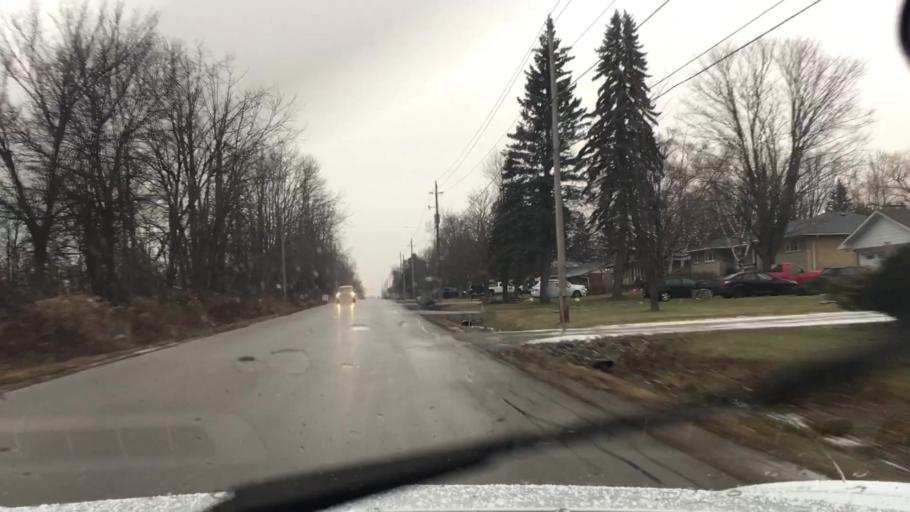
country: CA
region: Ontario
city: Oshawa
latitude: 43.8960
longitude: -78.7816
